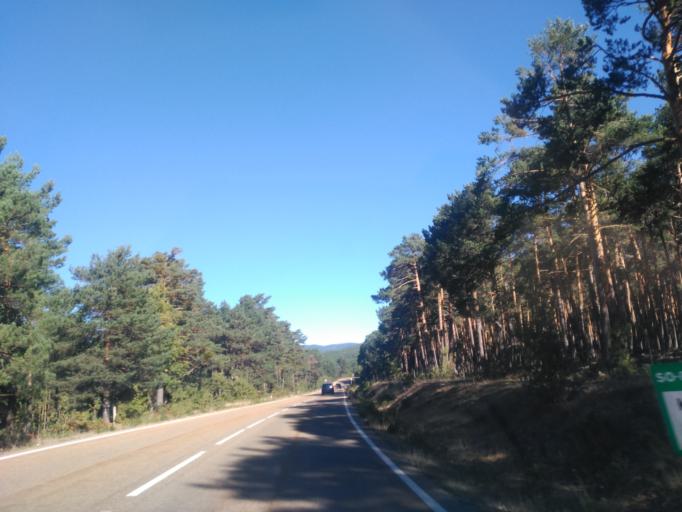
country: ES
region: Castille and Leon
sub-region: Provincia de Soria
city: Vinuesa
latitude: 41.9361
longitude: -2.7670
